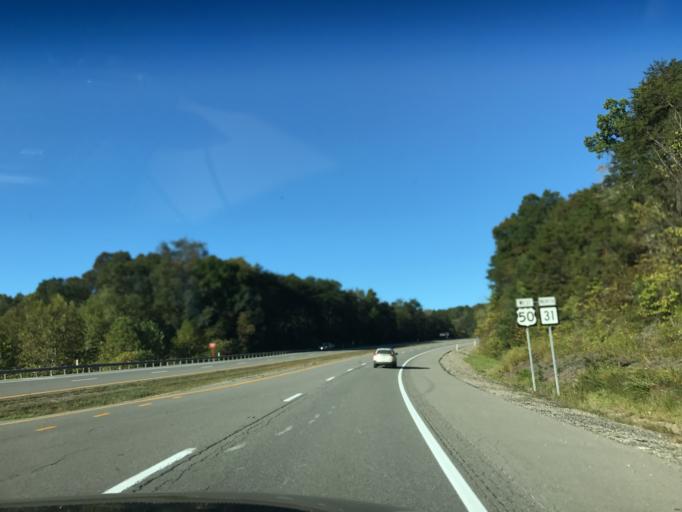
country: US
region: Ohio
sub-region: Washington County
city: Reno
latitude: 39.2503
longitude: -81.3051
